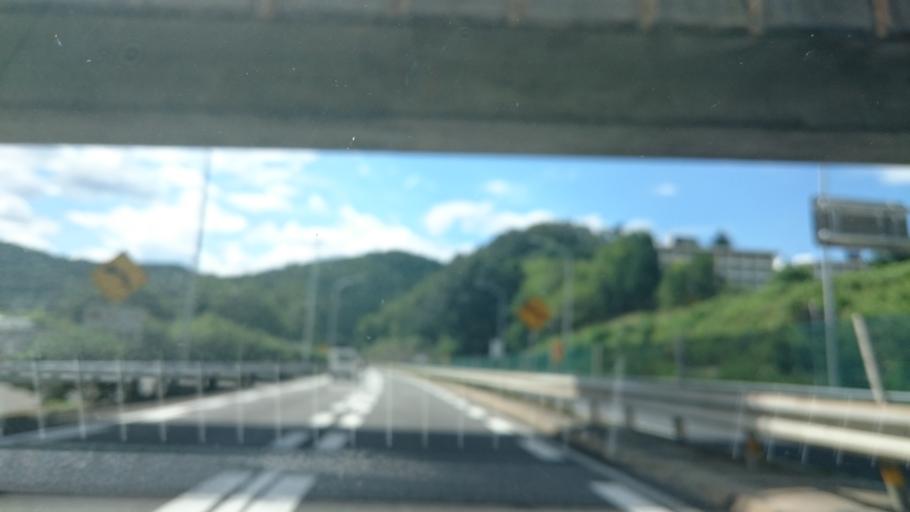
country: JP
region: Gifu
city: Nakatsugawa
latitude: 35.5181
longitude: 137.5708
